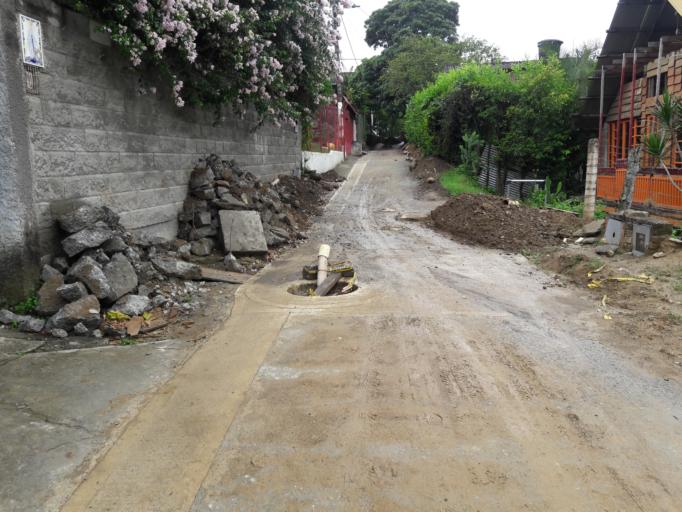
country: CO
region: Valle del Cauca
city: Cali
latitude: 3.4734
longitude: -76.5551
